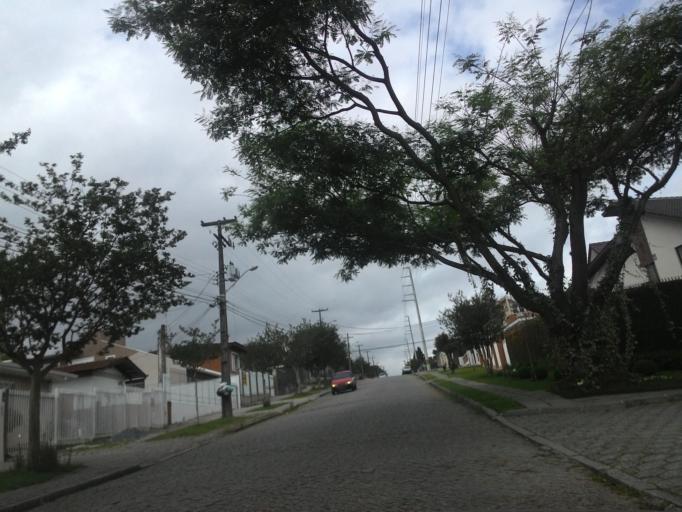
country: BR
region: Parana
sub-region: Curitiba
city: Curitiba
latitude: -25.4619
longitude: -49.2437
